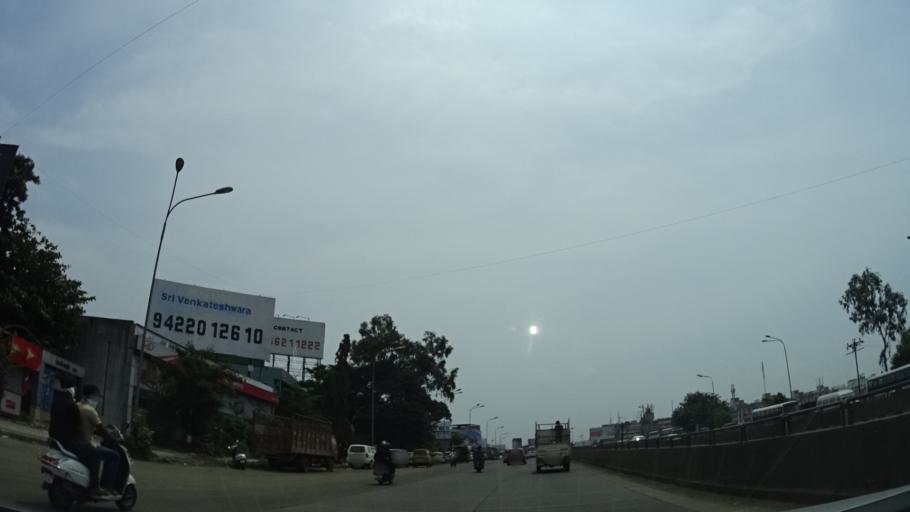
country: IN
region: Maharashtra
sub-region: Pune Division
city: Lohogaon
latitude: 18.5633
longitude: 73.9357
